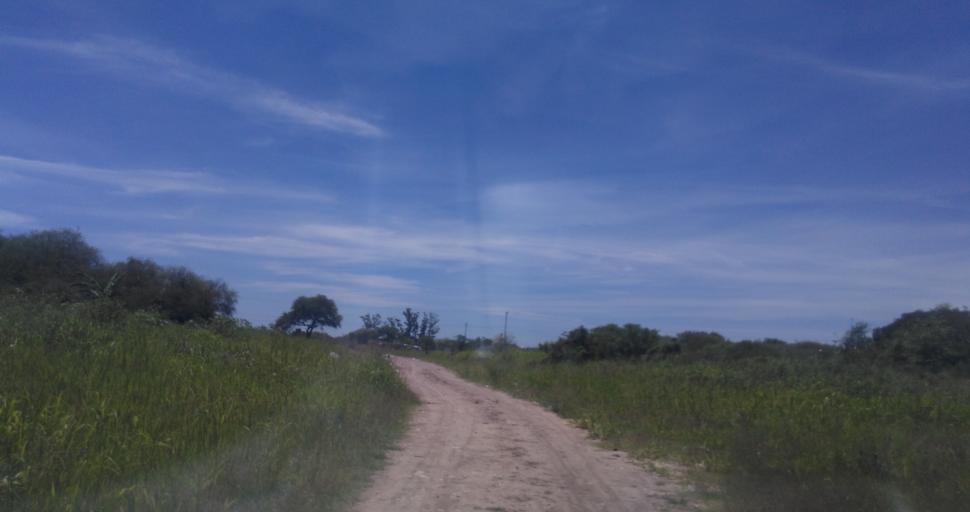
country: AR
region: Chaco
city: Fontana
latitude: -27.4256
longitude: -59.0460
